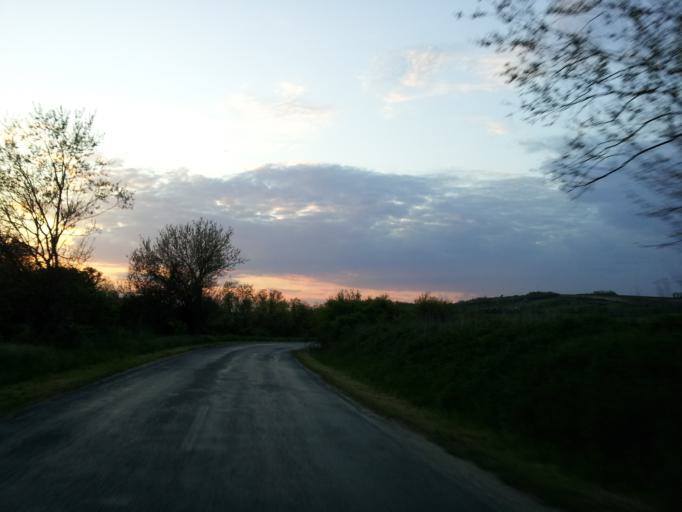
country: HU
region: Pest
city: Perbal
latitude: 47.6338
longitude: 18.7565
